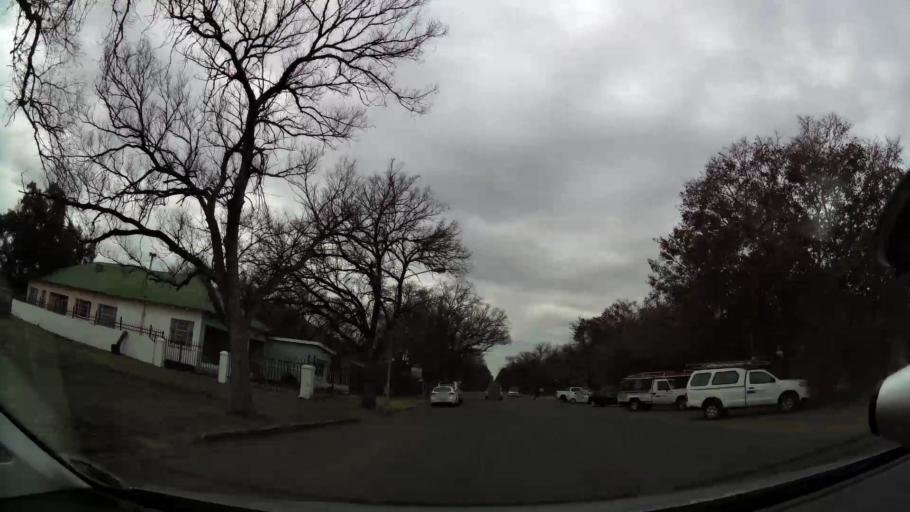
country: ZA
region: Orange Free State
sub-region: Fezile Dabi District Municipality
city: Kroonstad
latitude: -27.6624
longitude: 27.2414
